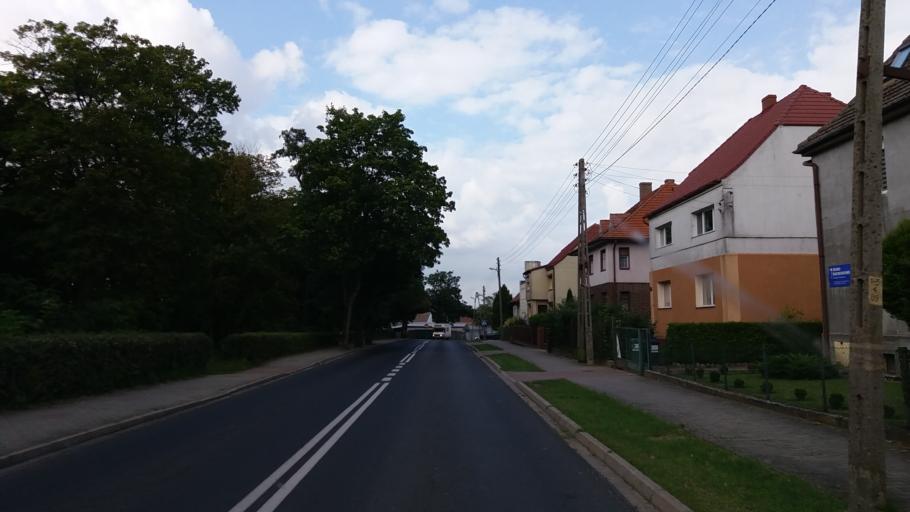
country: PL
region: West Pomeranian Voivodeship
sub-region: Powiat choszczenski
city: Pelczyce
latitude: 53.0371
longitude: 15.3002
